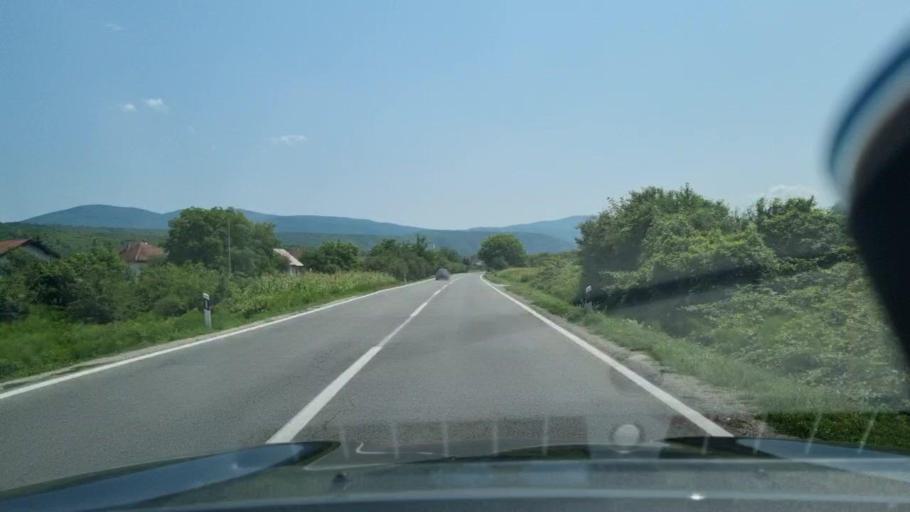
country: BA
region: Federation of Bosnia and Herzegovina
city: Bihac
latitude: 44.8054
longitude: 15.8973
